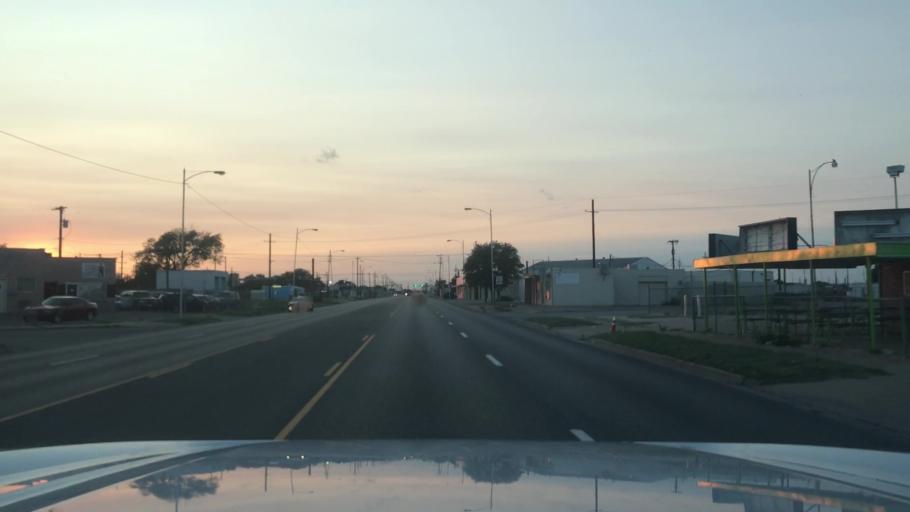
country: US
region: Texas
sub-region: Lubbock County
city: Lubbock
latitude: 33.5969
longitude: -101.8582
